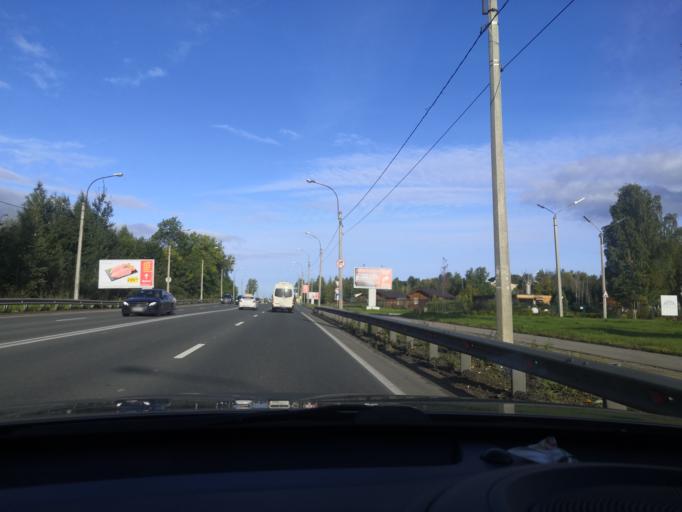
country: RU
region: St.-Petersburg
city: Pargolovo
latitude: 60.0737
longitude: 30.2806
